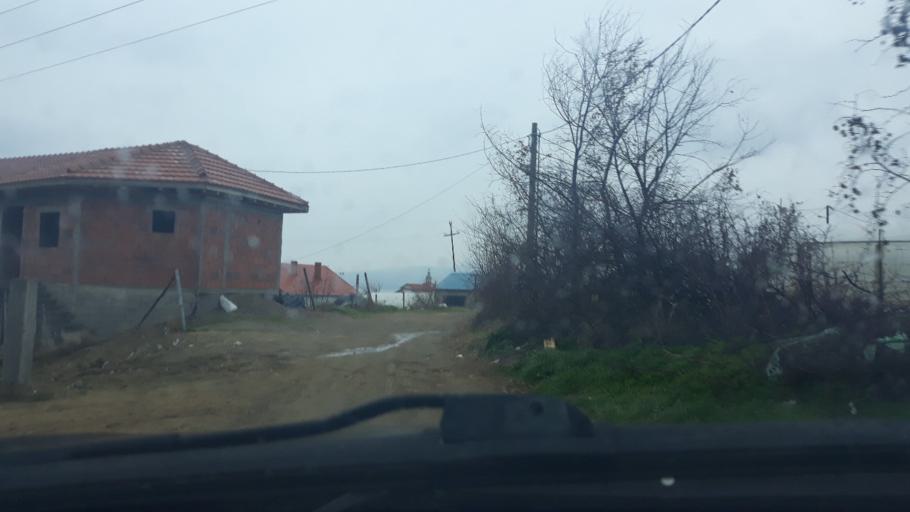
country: MK
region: Dojran
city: Star Dojran
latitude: 41.2639
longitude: 22.7502
